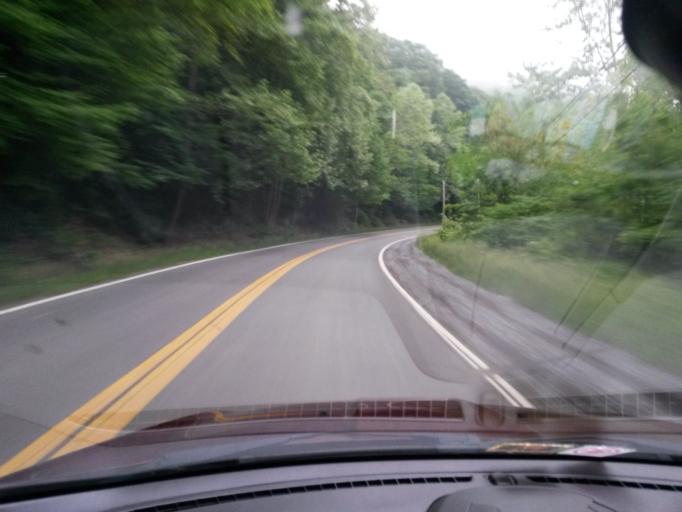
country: US
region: West Virginia
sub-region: Wyoming County
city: Pineville
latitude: 37.5266
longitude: -81.5913
